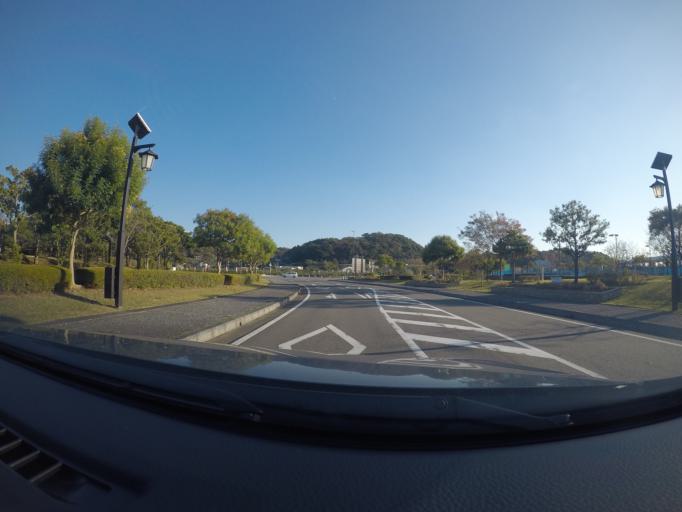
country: JP
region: Kumamoto
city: Minamata
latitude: 32.2006
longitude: 130.3820
